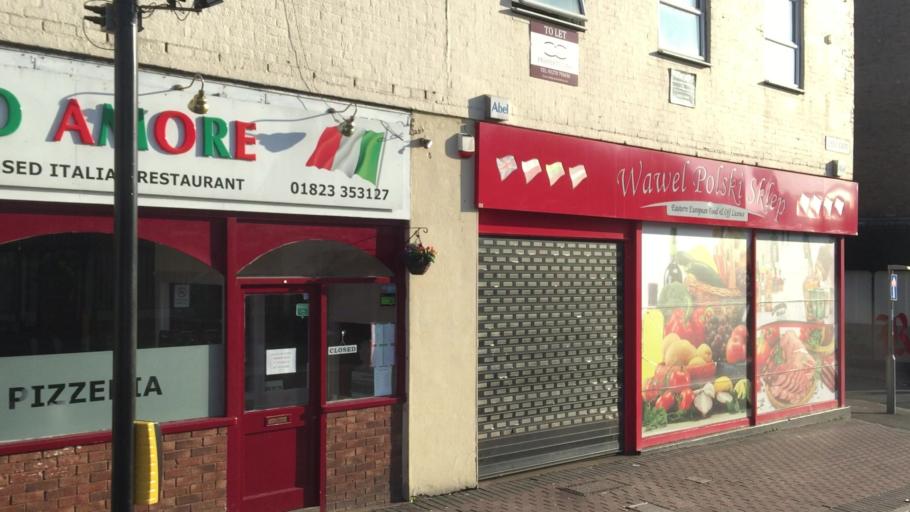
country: GB
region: England
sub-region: Somerset
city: Taunton
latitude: 51.0150
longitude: -3.0972
